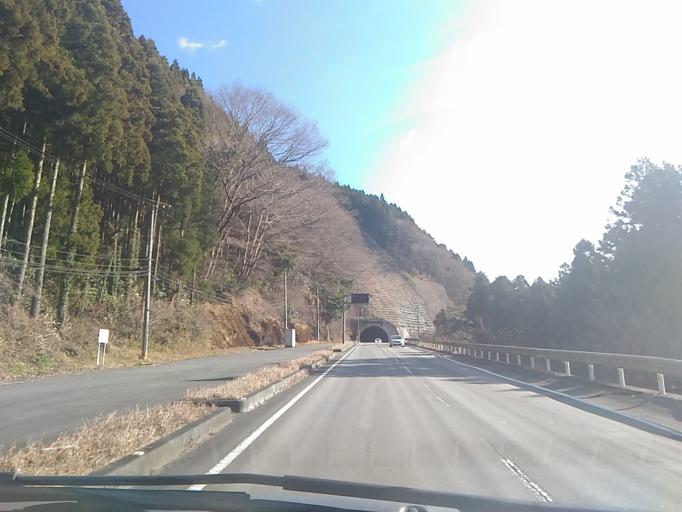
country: JP
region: Fukushima
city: Iwaki
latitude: 37.0086
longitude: 140.6868
